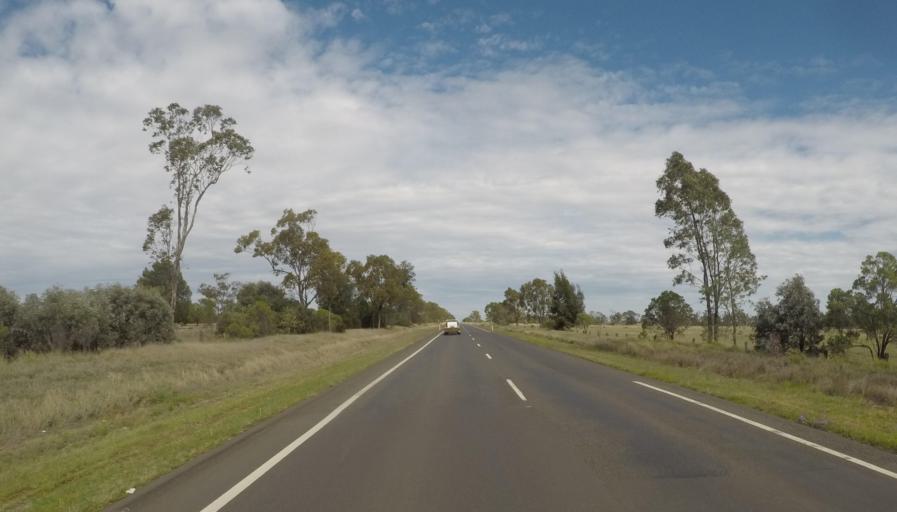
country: AU
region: Queensland
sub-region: Maranoa
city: Roma
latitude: -26.5860
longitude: 149.1517
